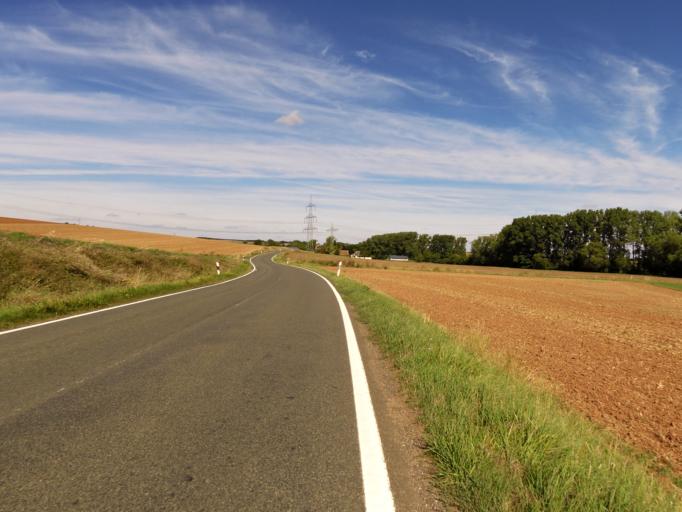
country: DE
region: Rheinland-Pfalz
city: Breunigweiler
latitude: 49.5813
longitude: 7.9700
